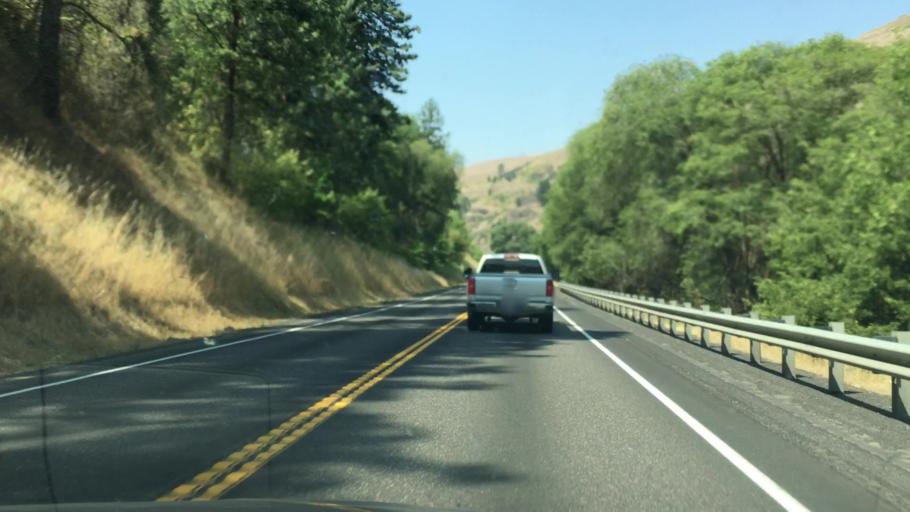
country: US
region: Idaho
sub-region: Nez Perce County
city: Lapwai
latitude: 46.4877
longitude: -116.7414
